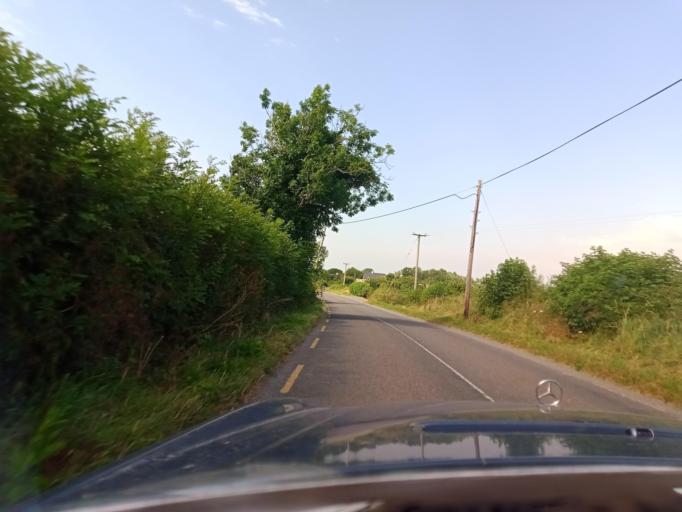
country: IE
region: Leinster
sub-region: Kilkenny
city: Callan
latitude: 52.5257
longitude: -7.3003
